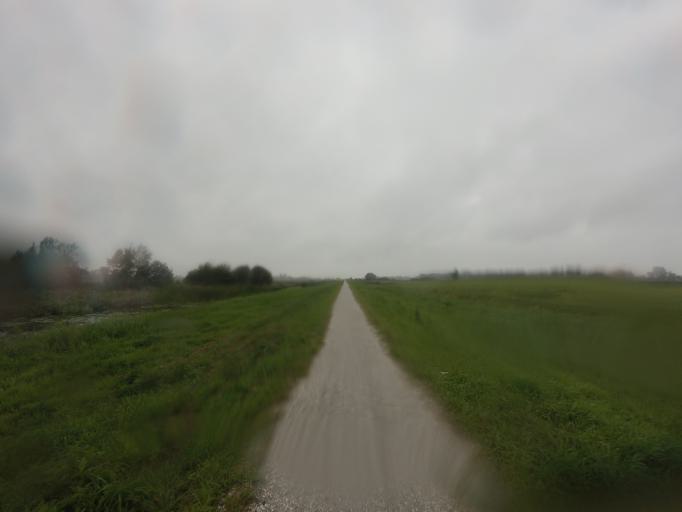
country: NL
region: Friesland
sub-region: Gemeente Smallingerland
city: Oudega
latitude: 53.1024
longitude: 5.9671
